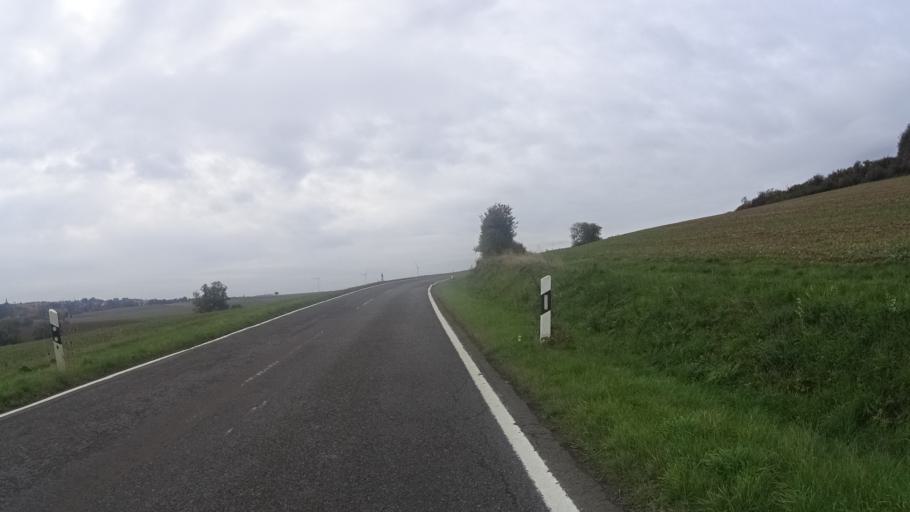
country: DE
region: Rheinland-Pfalz
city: Ottersheim
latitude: 49.6204
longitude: 8.1032
